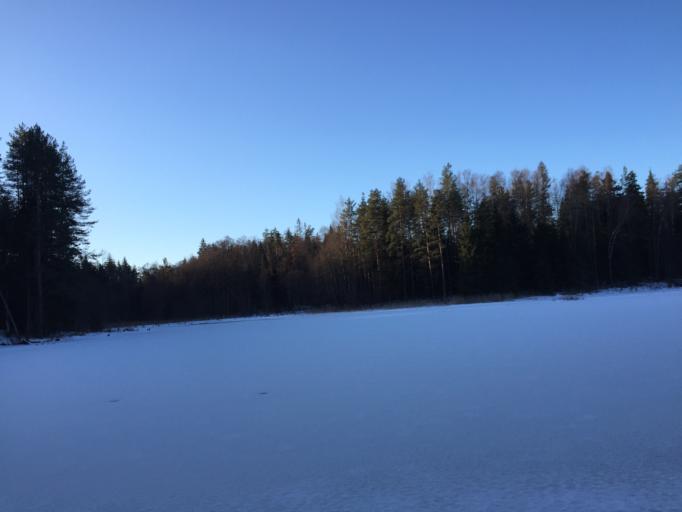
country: LV
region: Kegums
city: Kegums
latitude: 56.7292
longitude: 24.6407
